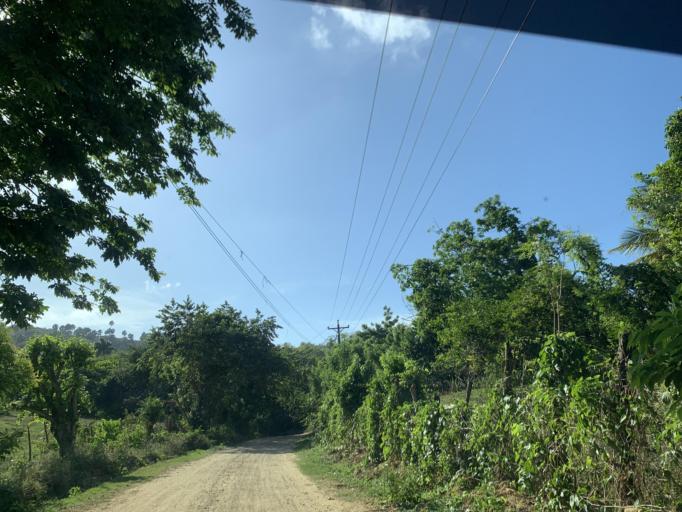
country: DO
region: Puerto Plata
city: Luperon
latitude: 19.8892
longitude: -70.8881
